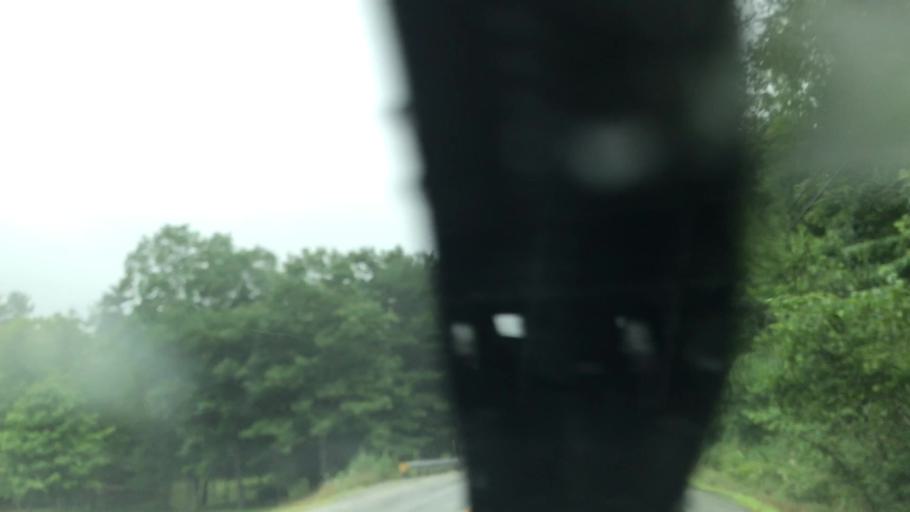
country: US
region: Maine
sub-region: York County
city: North Berwick
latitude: 43.2992
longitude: -70.7587
